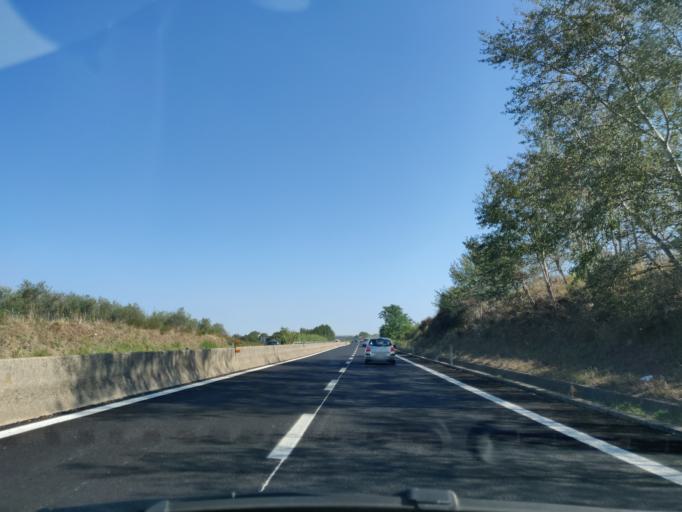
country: IT
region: Latium
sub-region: Provincia di Viterbo
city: Viterbo
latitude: 42.4061
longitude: 12.0701
